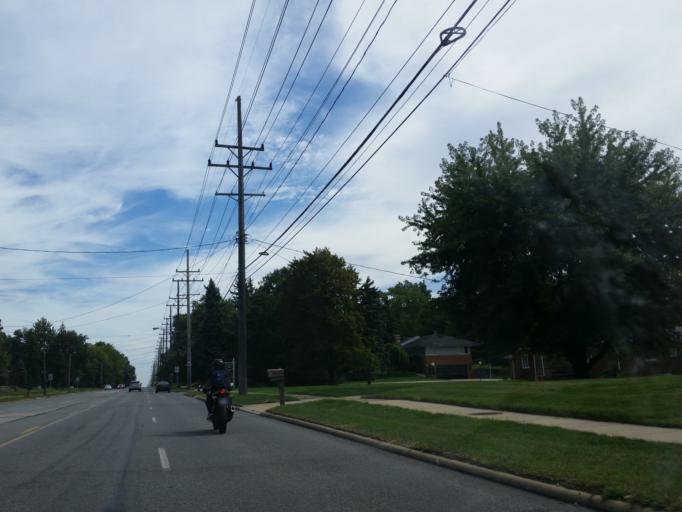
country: US
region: Ohio
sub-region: Cuyahoga County
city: Seven Hills
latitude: 41.3615
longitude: -81.6813
